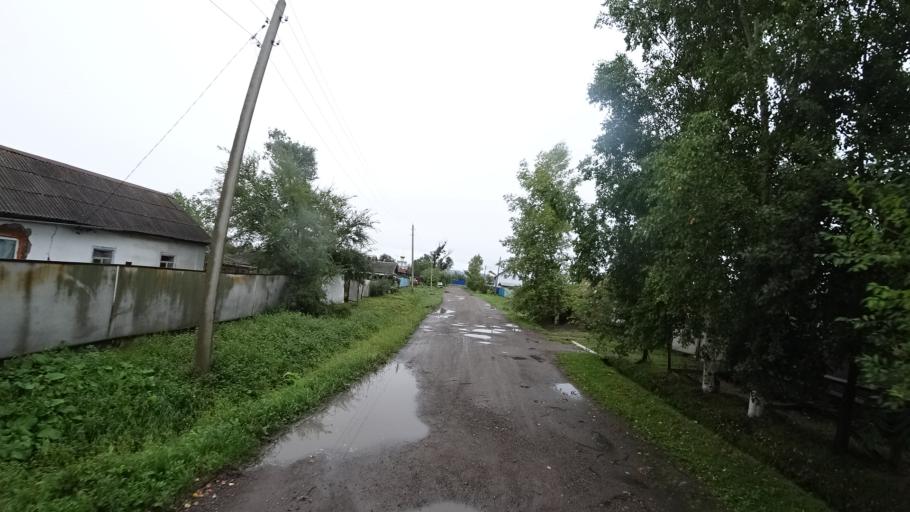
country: RU
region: Primorskiy
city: Monastyrishche
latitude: 44.2062
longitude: 132.4519
